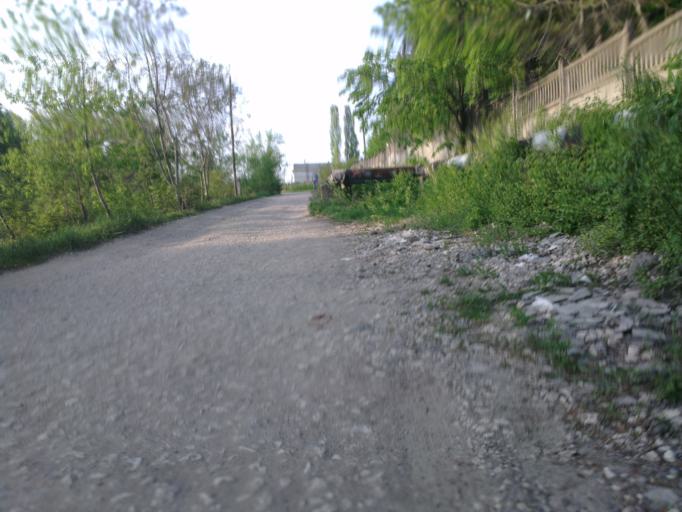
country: MD
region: Chisinau
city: Stauceni
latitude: 47.0608
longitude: 28.8865
